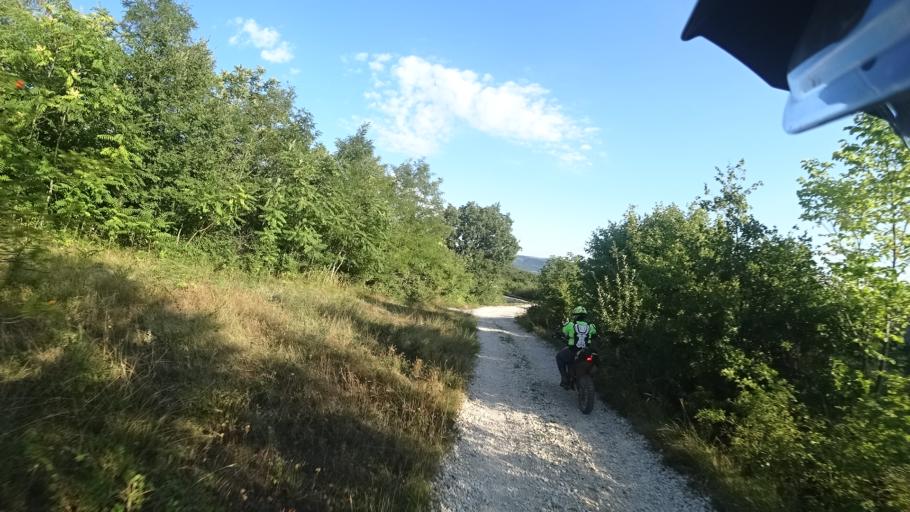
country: HR
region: Sibensko-Kniniska
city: Knin
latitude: 44.1538
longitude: 16.0933
